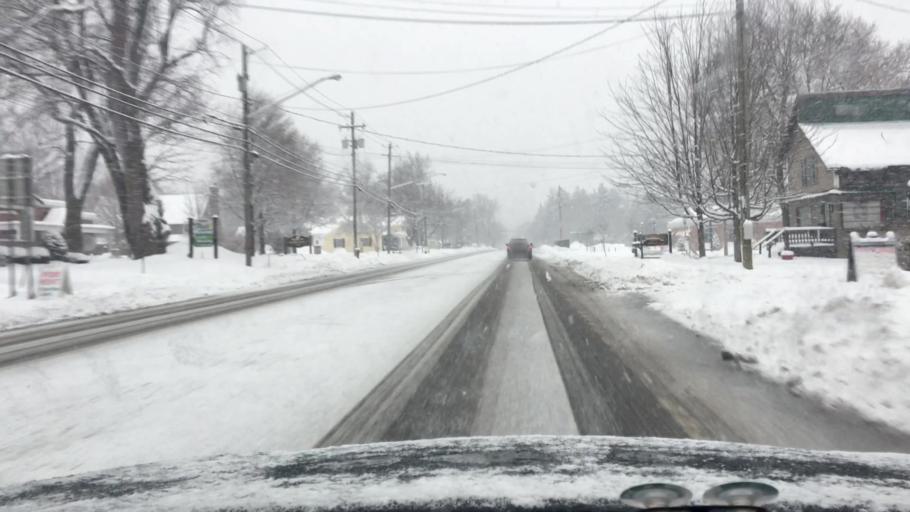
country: US
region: New York
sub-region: Erie County
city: Orchard Park
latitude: 42.7782
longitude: -78.7454
